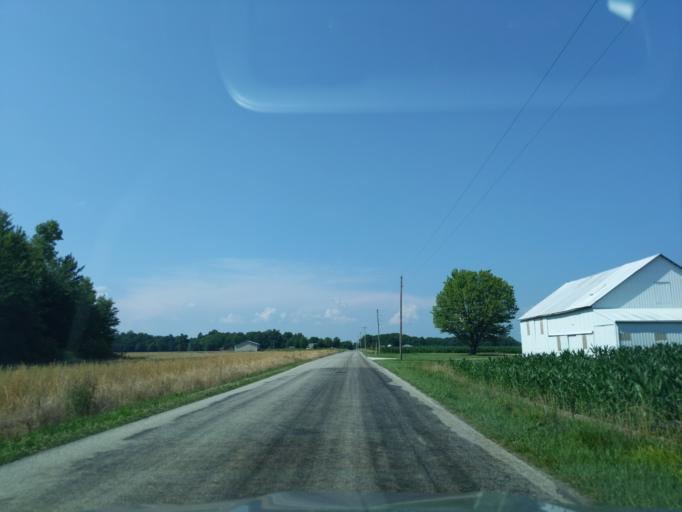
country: US
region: Indiana
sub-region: Ripley County
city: Osgood
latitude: 39.1420
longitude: -85.3393
